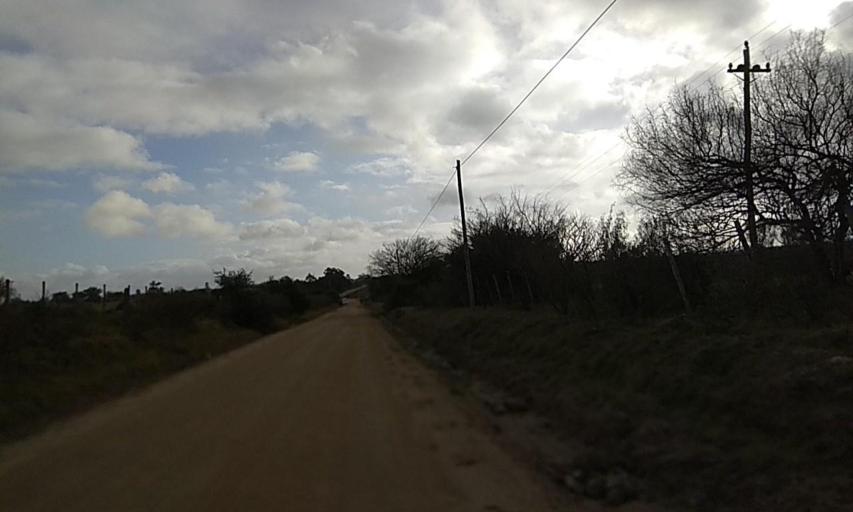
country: UY
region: Florida
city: Florida
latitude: -34.0663
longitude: -56.1937
